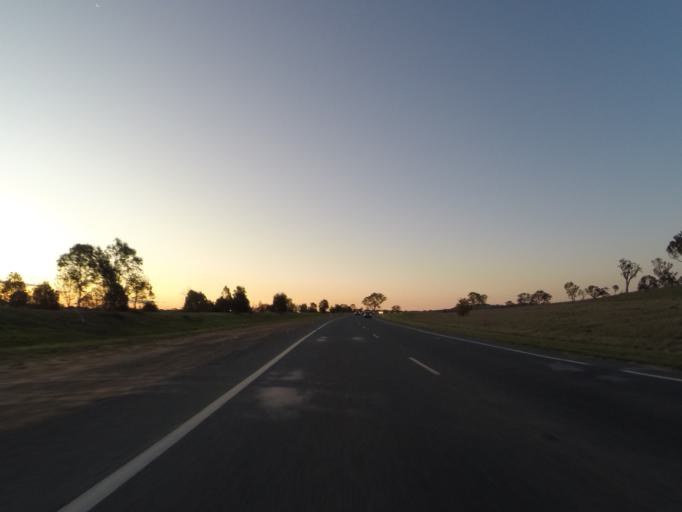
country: AU
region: Australian Capital Territory
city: Kaleen
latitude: -35.1986
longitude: 149.1637
